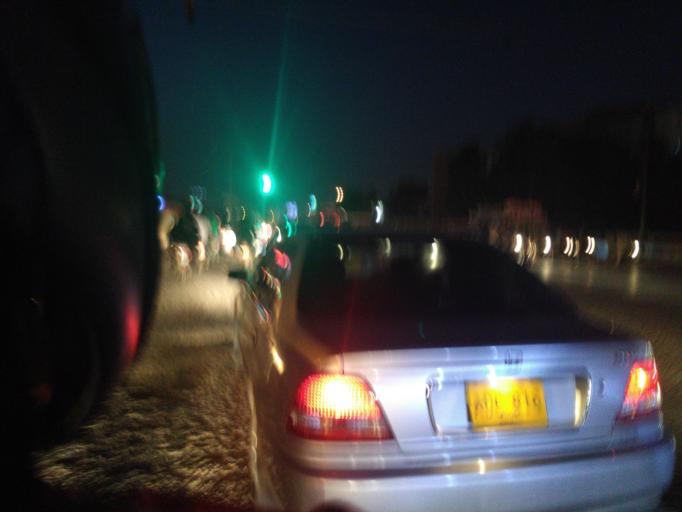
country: PK
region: Sindh
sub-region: Karachi District
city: Karachi
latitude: 24.8408
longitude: 67.0602
